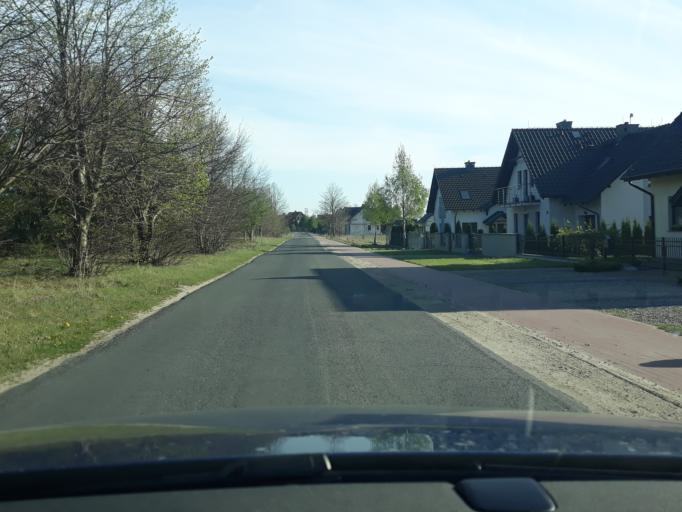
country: PL
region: Pomeranian Voivodeship
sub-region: Powiat czluchowski
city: Przechlewo
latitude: 53.8299
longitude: 17.3771
